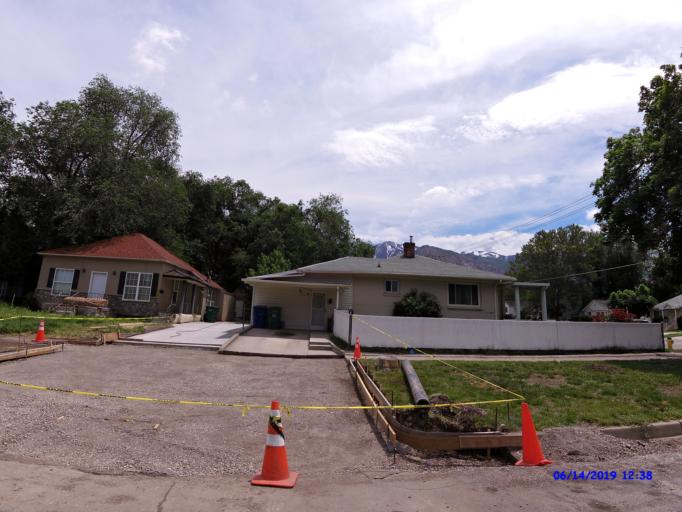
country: US
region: Utah
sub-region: Weber County
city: Ogden
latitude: 41.2164
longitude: -111.9538
